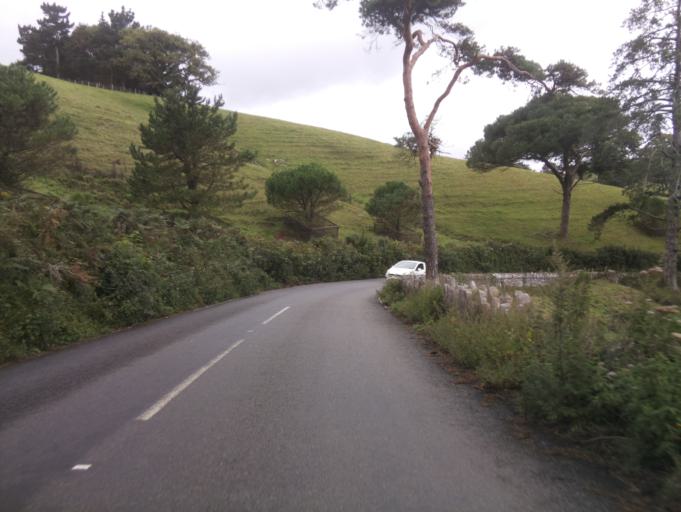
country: GB
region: England
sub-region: Devon
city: Dartmouth
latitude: 50.3182
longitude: -3.6146
